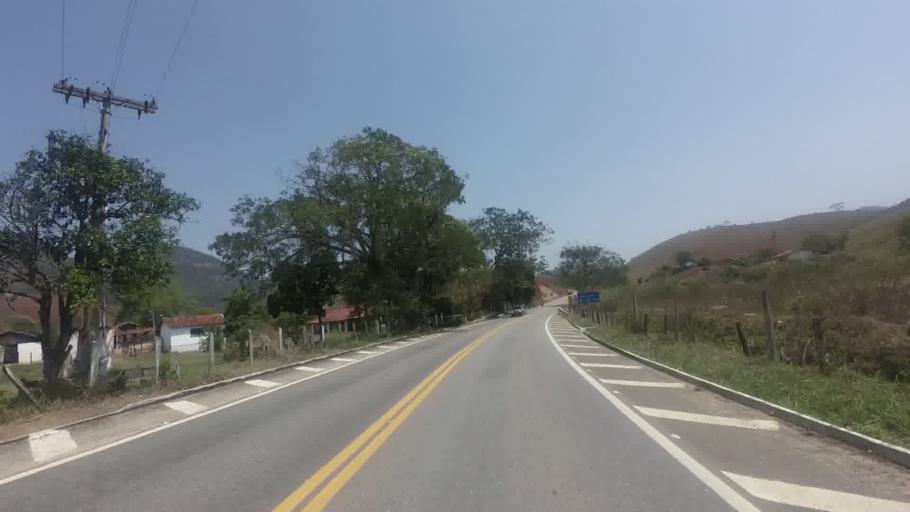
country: BR
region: Espirito Santo
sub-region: Jeronimo Monteiro
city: Jeronimo Monteiro
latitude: -20.9029
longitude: -41.2926
